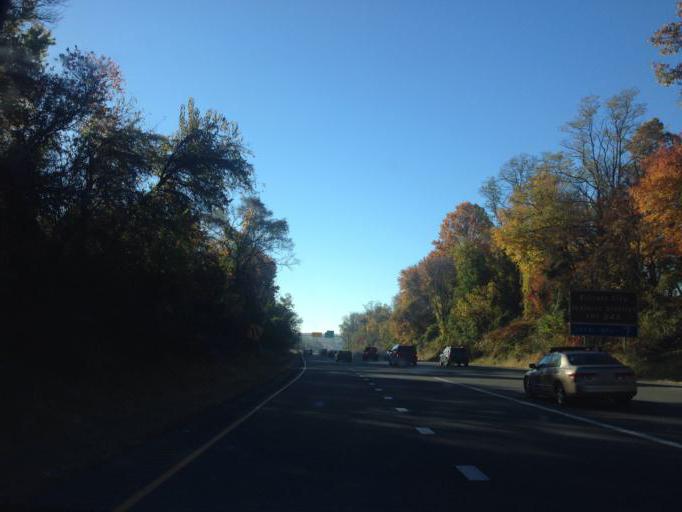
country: US
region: Maryland
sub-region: Howard County
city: Ellicott City
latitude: 39.2885
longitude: -76.8261
